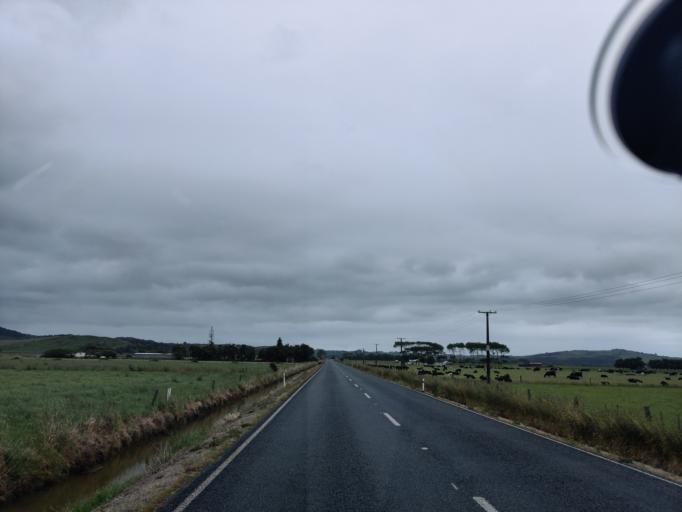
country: NZ
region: Northland
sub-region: Kaipara District
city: Dargaville
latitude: -36.1191
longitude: 174.0662
